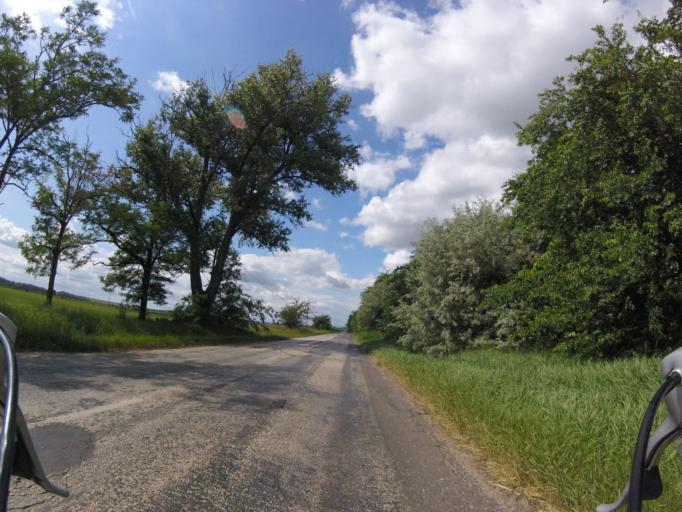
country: HU
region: Fejer
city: Seregelyes
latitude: 47.1382
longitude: 18.5768
